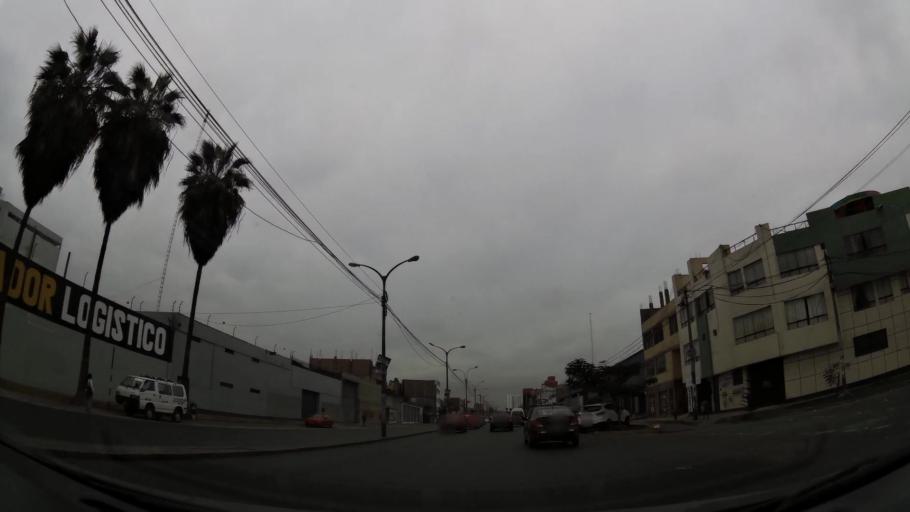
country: PE
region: Lima
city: Lima
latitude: -12.0484
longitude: -77.0620
